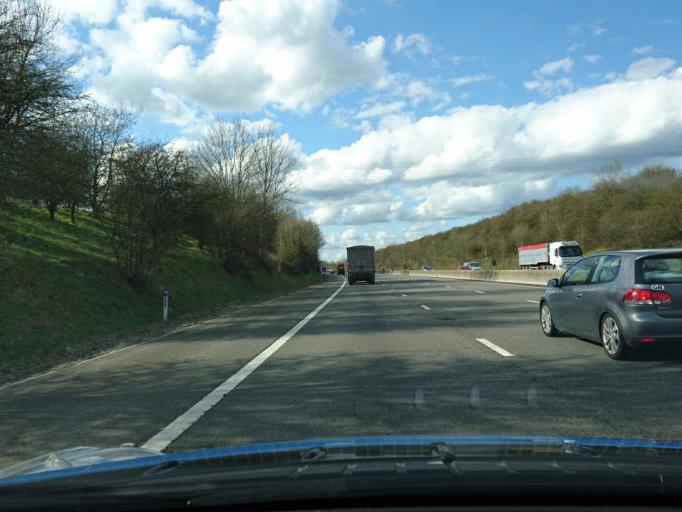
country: GB
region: England
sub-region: Wiltshire
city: Aldbourne
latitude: 51.4981
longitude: -1.5846
